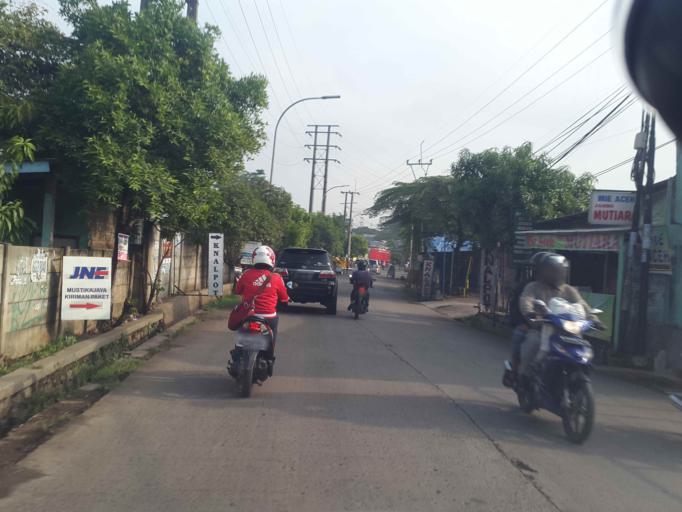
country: ID
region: West Java
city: Bekasi
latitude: -6.2896
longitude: 107.0326
